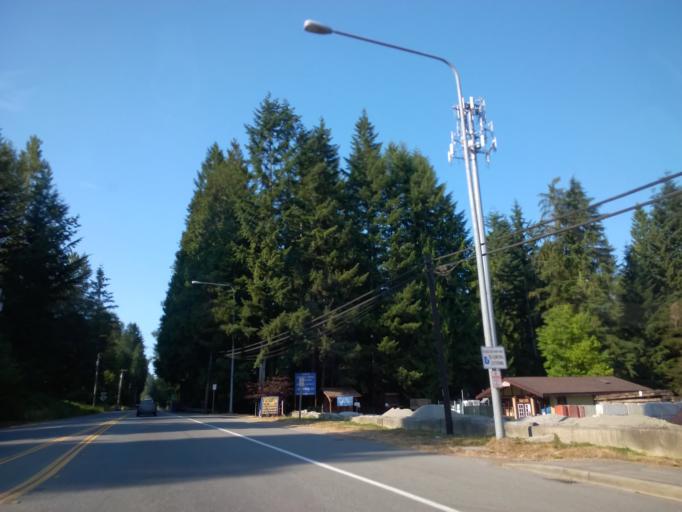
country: US
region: Washington
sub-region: King County
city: Cottage Lake
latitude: 47.7193
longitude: -122.0872
